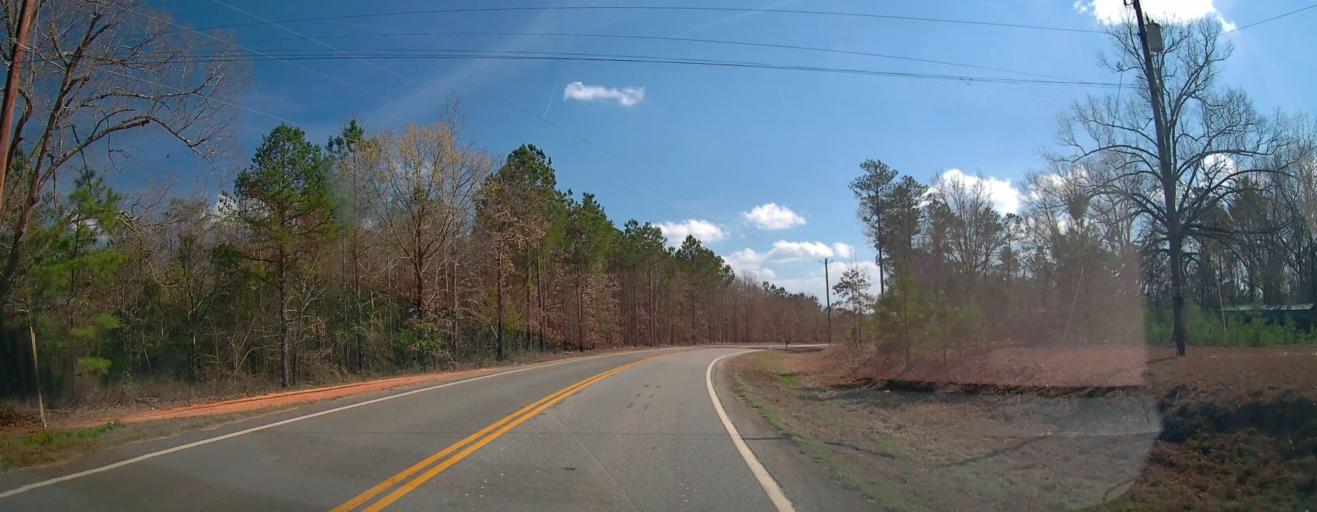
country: US
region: Georgia
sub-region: Wilkinson County
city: Gordon
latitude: 32.8390
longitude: -83.3306
